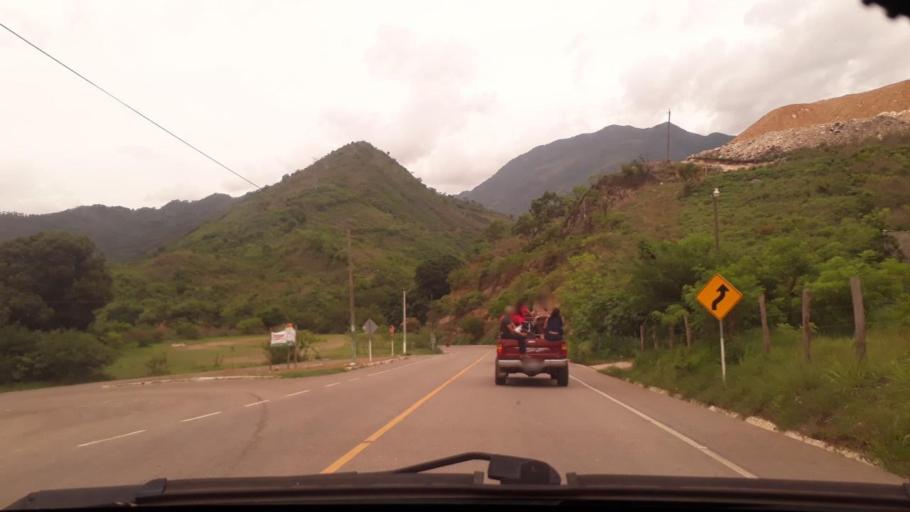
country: GT
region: Chiquimula
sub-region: Municipio de Camotan
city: Camotan
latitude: 14.8205
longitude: -89.3641
